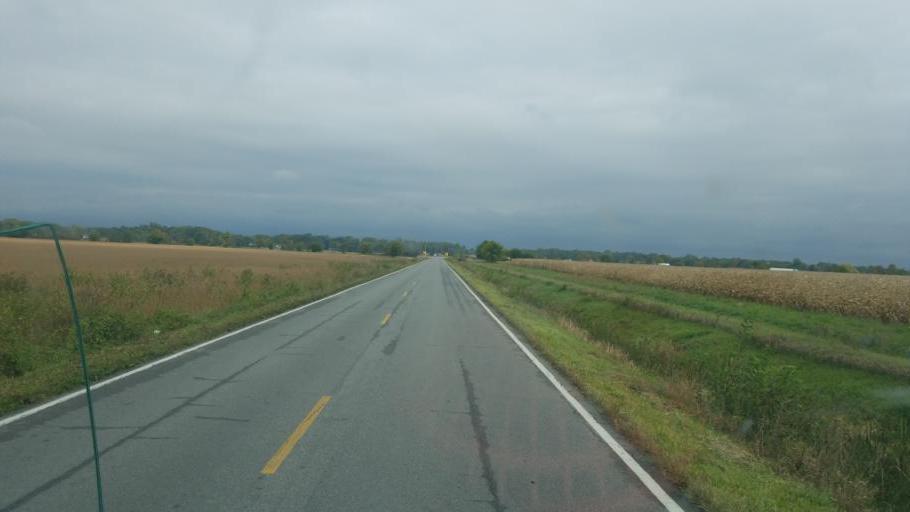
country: US
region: Ohio
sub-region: Wood County
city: Bowling Green
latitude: 41.3447
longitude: -83.6698
